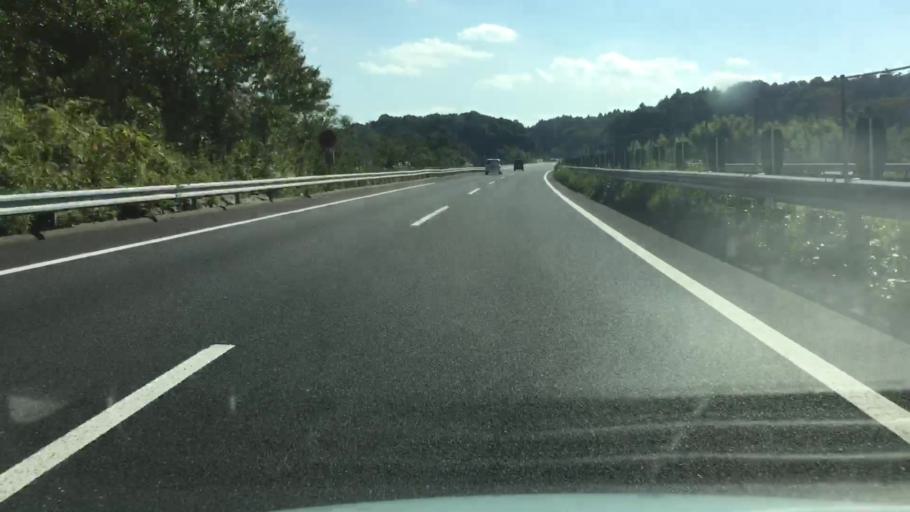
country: JP
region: Ibaraki
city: Tomobe
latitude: 36.3436
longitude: 140.2620
